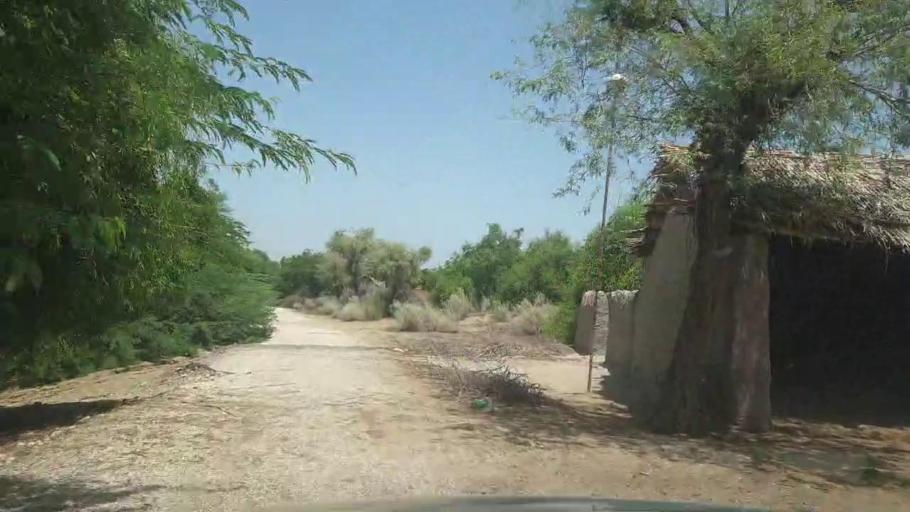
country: PK
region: Sindh
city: Kot Diji
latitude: 27.3183
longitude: 69.0610
